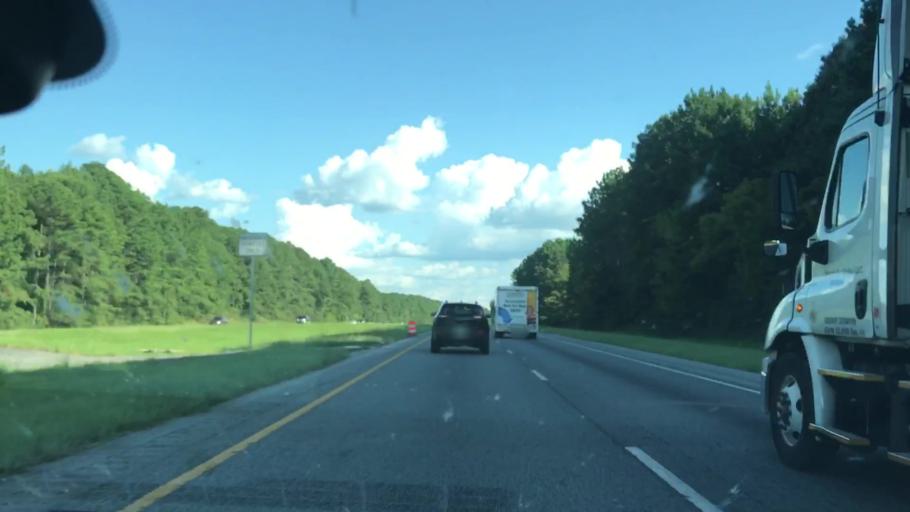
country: US
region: Georgia
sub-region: Harris County
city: Hamilton
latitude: 32.6286
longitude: -84.9599
